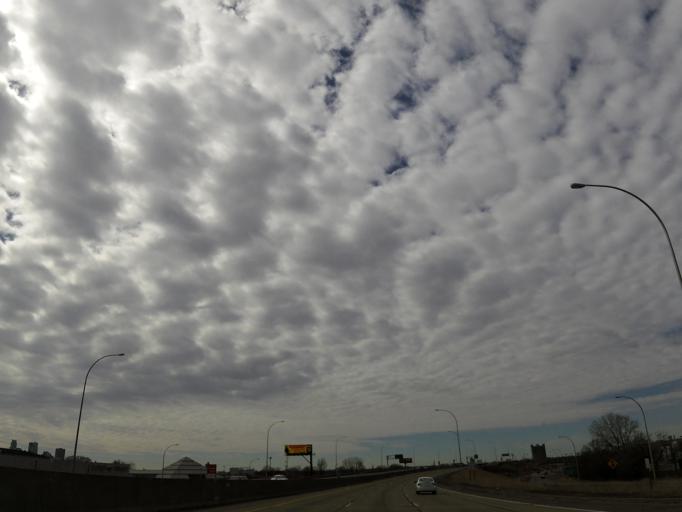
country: US
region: Minnesota
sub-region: Ramsey County
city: Lauderdale
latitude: 45.0009
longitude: -93.2229
